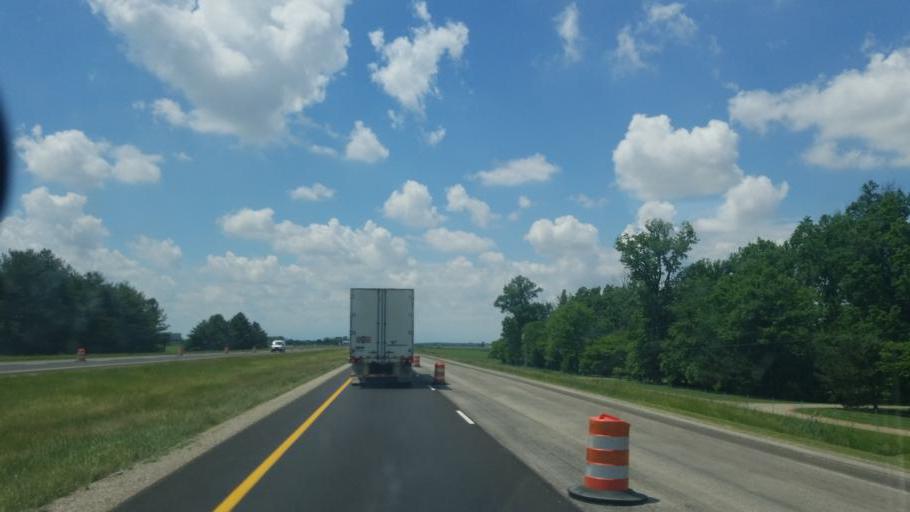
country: US
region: Indiana
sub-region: Allen County
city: Monroeville
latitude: 40.9952
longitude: -84.7955
